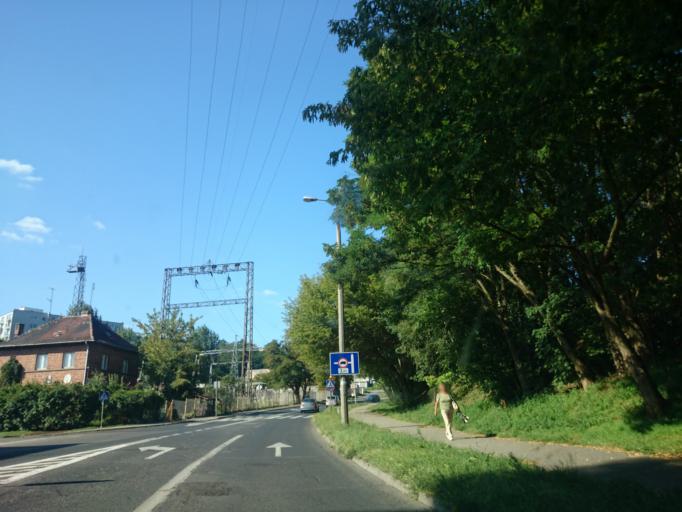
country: PL
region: Lubusz
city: Gorzow Wielkopolski
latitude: 52.7272
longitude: 15.2101
